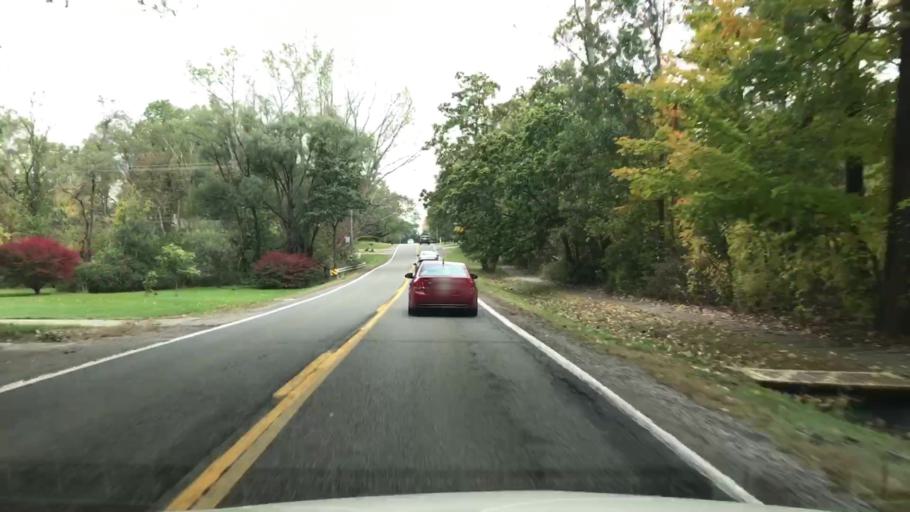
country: US
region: Michigan
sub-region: Macomb County
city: Shelby
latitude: 42.6795
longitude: -83.0667
